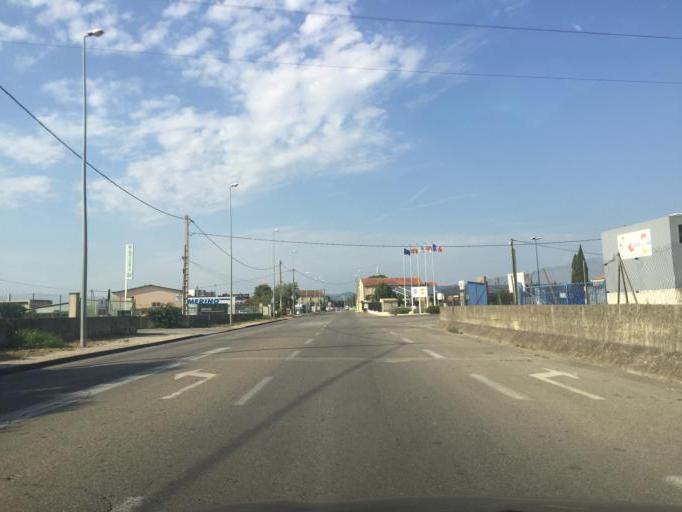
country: FR
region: Provence-Alpes-Cote d'Azur
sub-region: Departement du Vaucluse
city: Carpentras
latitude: 44.0362
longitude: 5.0400
